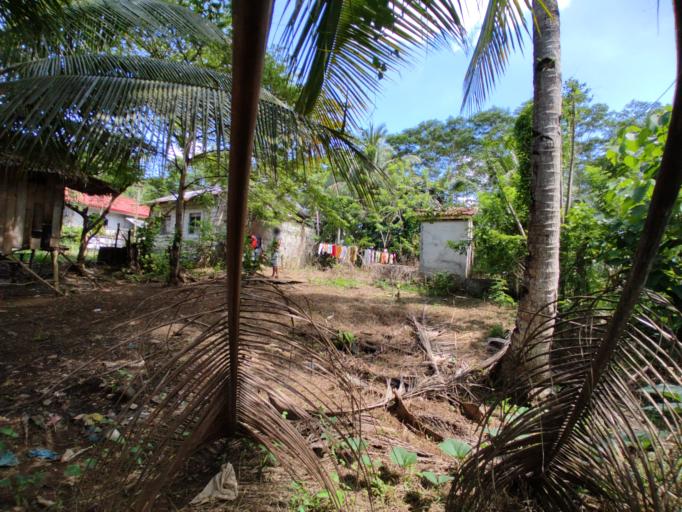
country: PH
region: Caraga
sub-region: Province of Agusan del Sur
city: Bayugan
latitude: 8.7324
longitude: 125.7513
